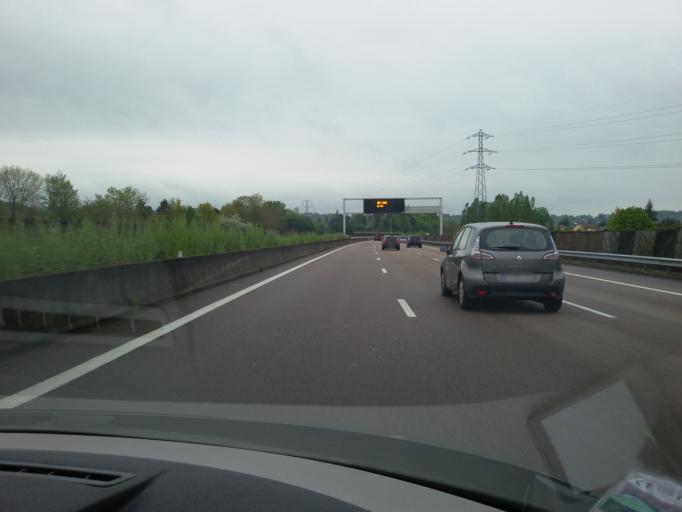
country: FR
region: Bourgogne
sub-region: Departement de Saone-et-Loire
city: Tournus
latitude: 46.5540
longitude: 4.9038
